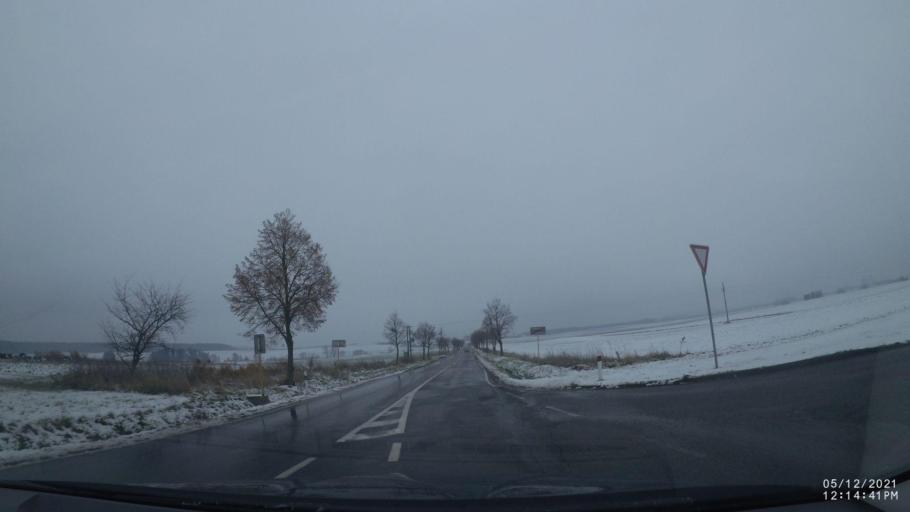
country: CZ
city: Ceske Mezirici
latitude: 50.3061
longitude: 16.0345
